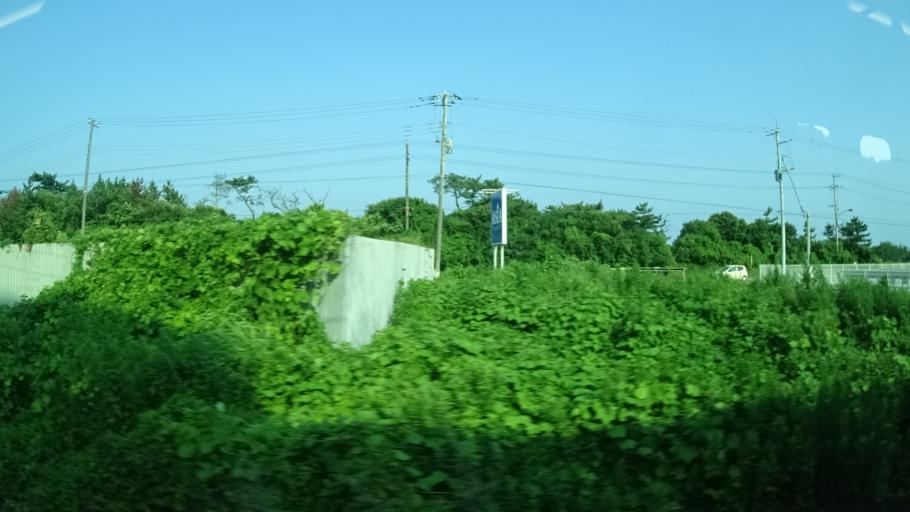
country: JP
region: Ibaraki
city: Kitaibaraki
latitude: 36.8125
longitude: 140.7637
